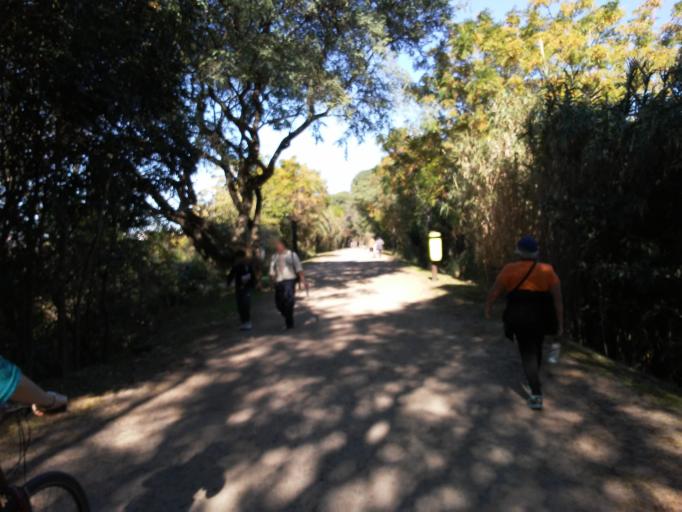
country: AR
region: Buenos Aires F.D.
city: Buenos Aires
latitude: -34.6136
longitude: -58.3560
